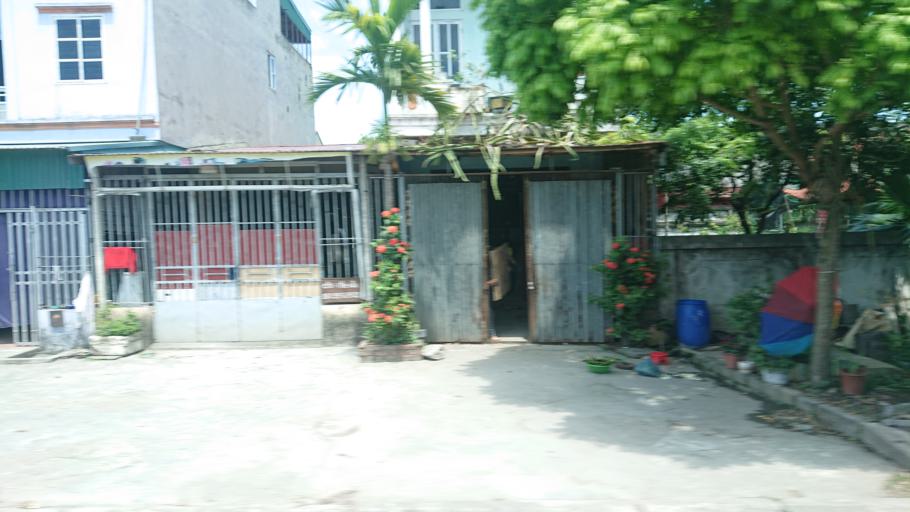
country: VN
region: Ha Nam
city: Thanh Pho Phu Ly
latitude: 20.5364
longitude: 105.9453
